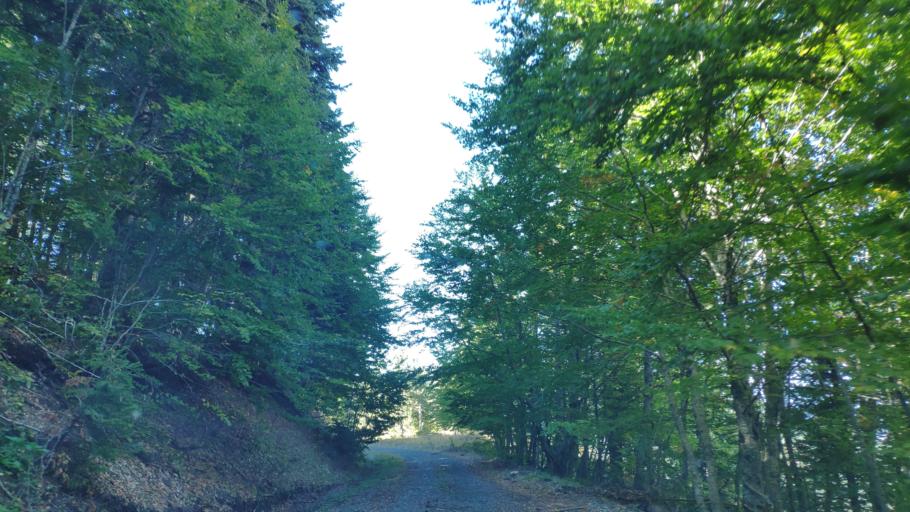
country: GR
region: Epirus
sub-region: Nomos Ioanninon
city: Metsovo
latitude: 39.8907
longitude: 21.2142
